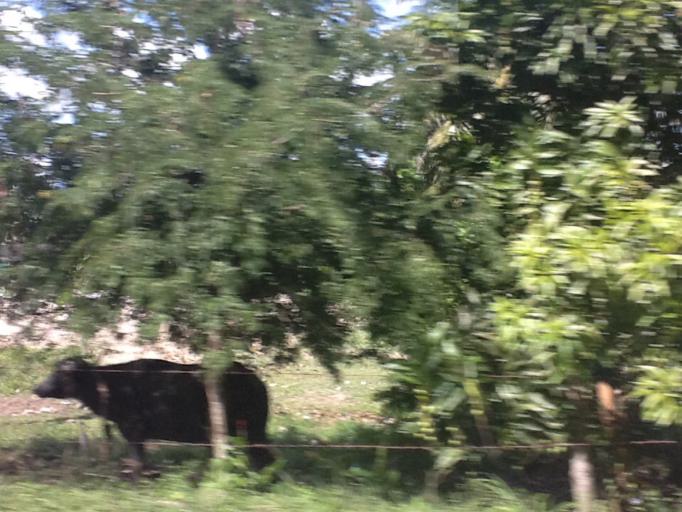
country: TH
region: Phuket
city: Thalang
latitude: 8.1245
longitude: 98.3206
